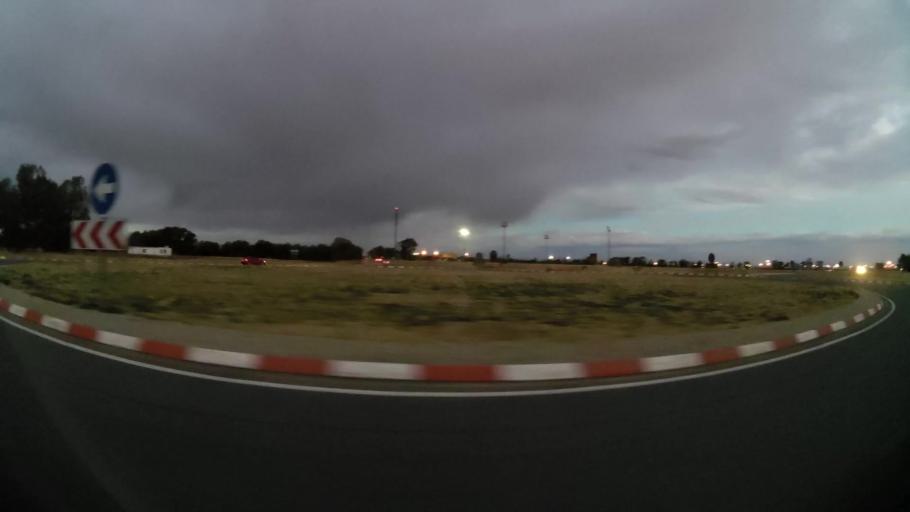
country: ZA
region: Orange Free State
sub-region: Lejweleputswa District Municipality
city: Welkom
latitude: -27.9374
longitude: 26.7873
